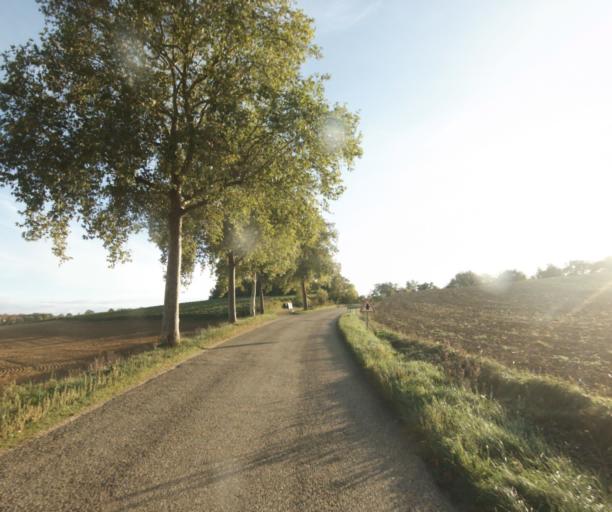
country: FR
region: Midi-Pyrenees
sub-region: Departement du Gers
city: Gondrin
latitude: 43.8796
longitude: 0.2874
